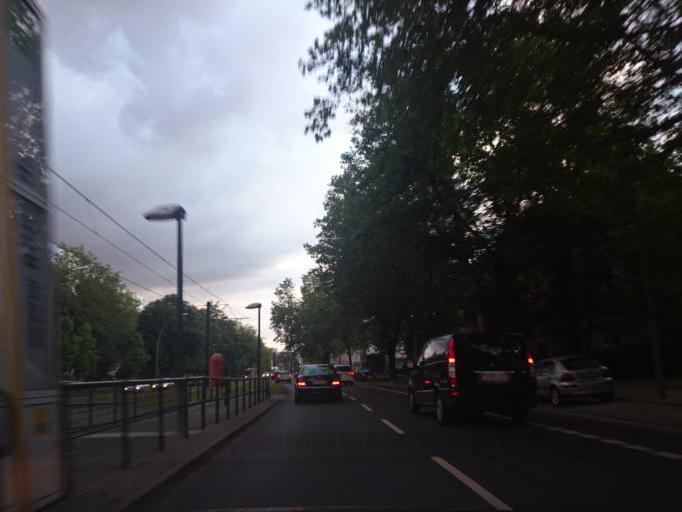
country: DE
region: Berlin
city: Friedrichsfelde
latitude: 52.5016
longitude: 13.5217
